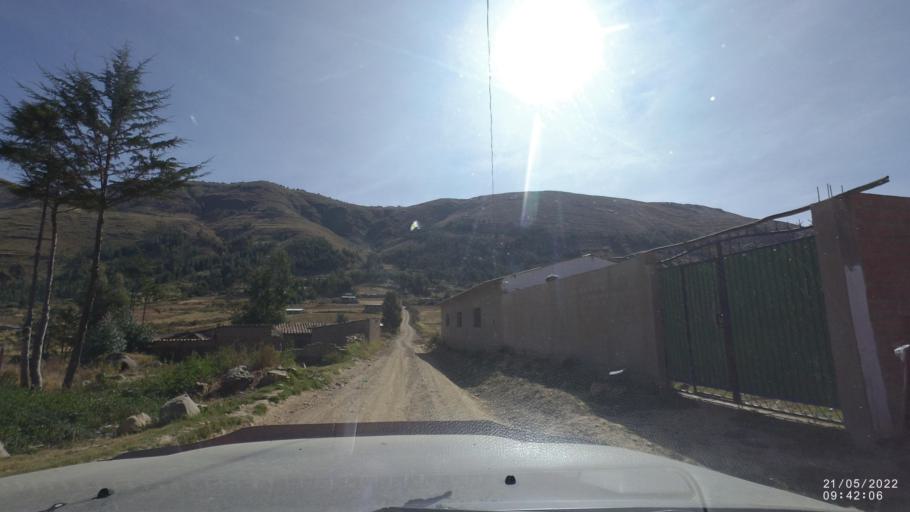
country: BO
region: Cochabamba
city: Colomi
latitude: -17.3429
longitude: -66.0116
